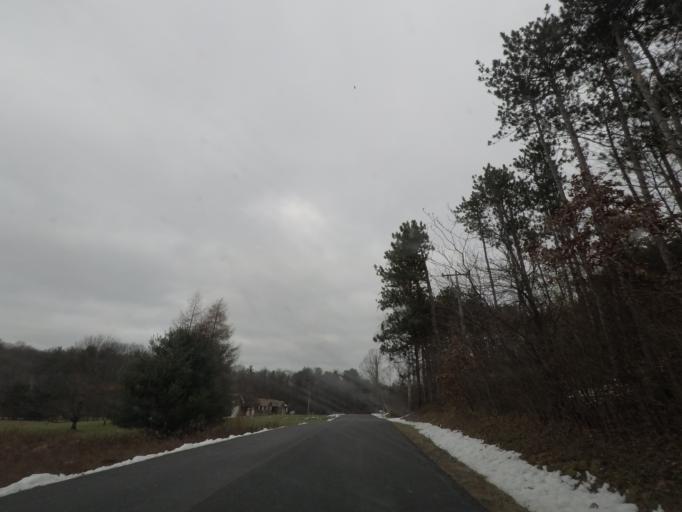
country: US
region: New York
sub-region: Rensselaer County
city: East Greenbush
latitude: 42.5873
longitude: -73.6448
